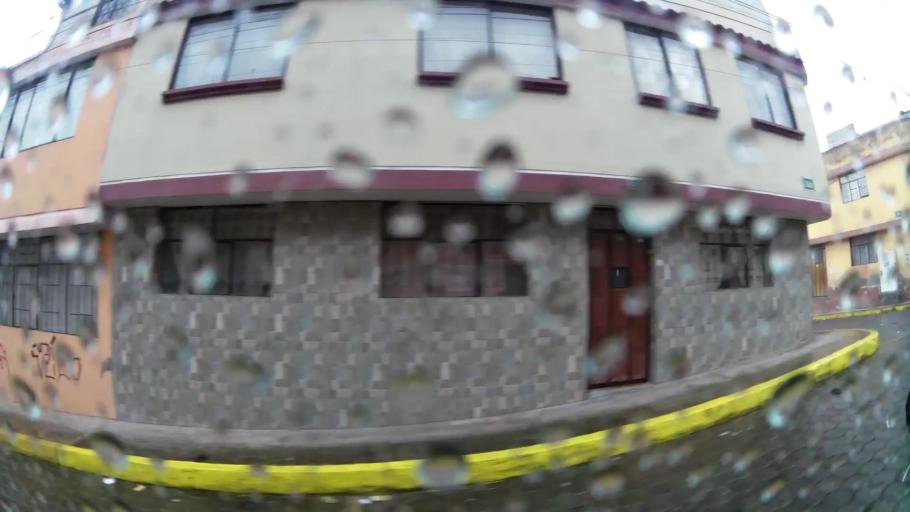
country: EC
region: Pichincha
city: Quito
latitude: -0.3222
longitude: -78.5549
